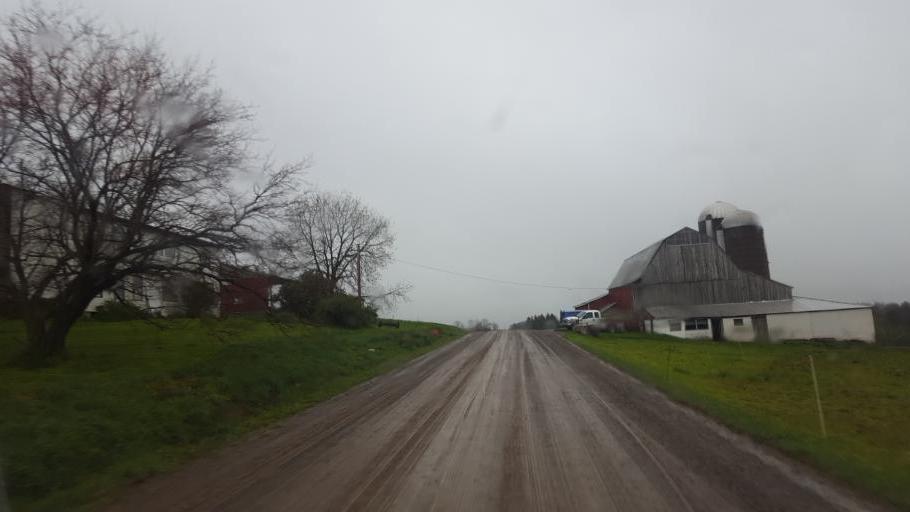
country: US
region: Pennsylvania
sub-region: Tioga County
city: Westfield
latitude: 42.0585
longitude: -77.4760
